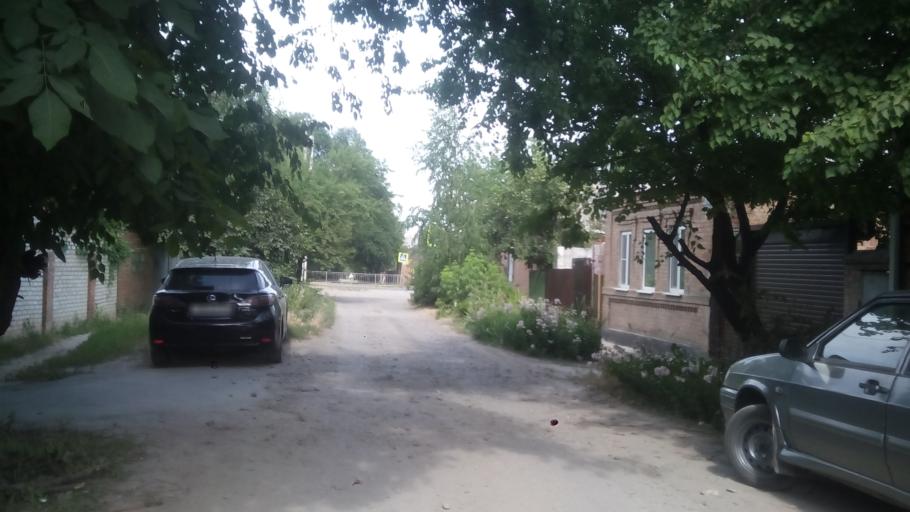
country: RU
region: Rostov
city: Rostov-na-Donu
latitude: 47.2257
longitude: 39.6406
